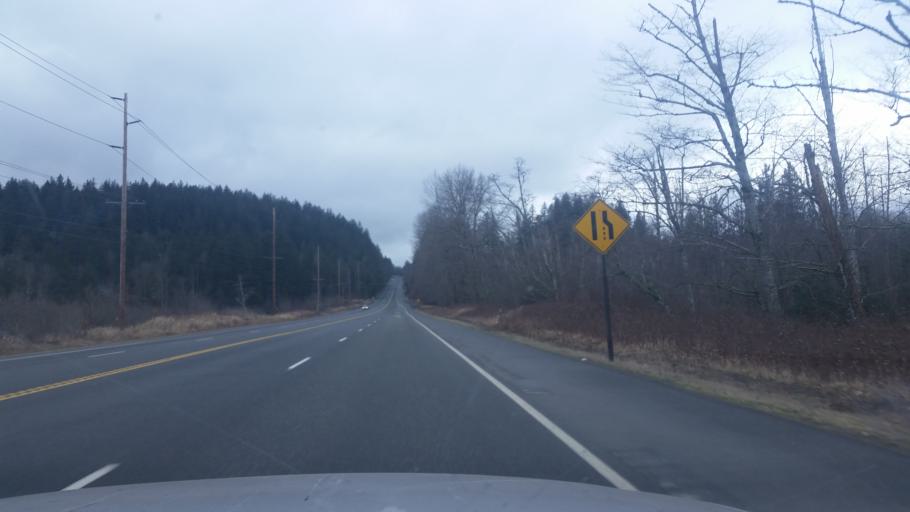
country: US
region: Washington
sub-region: King County
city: Snoqualmie
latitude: 47.5080
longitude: -121.8151
